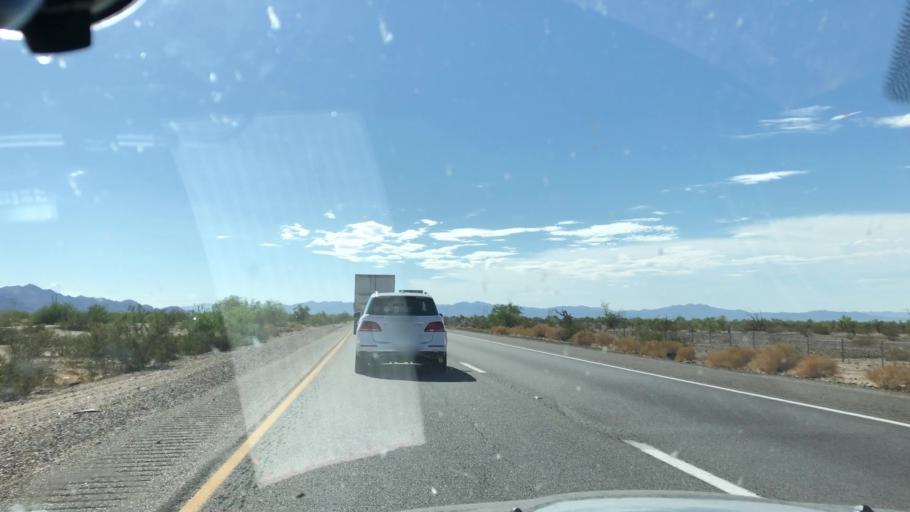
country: US
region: California
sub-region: Riverside County
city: Mesa Verde
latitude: 33.6741
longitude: -115.2149
